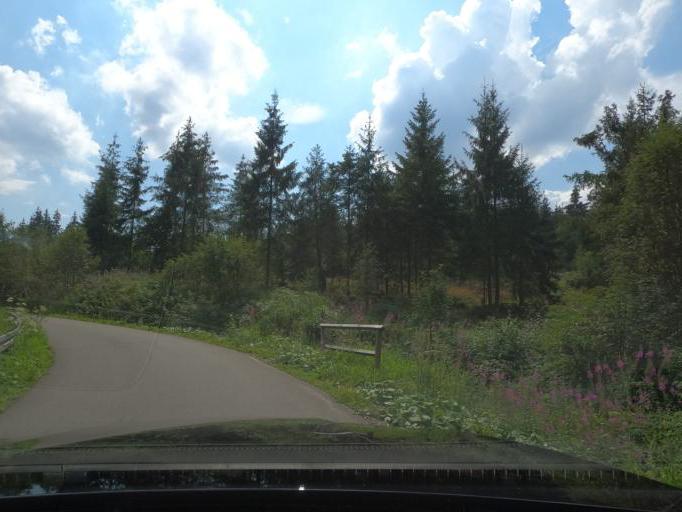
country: DE
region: Lower Saxony
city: Clausthal-Zellerfeld
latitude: 51.7743
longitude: 10.3063
